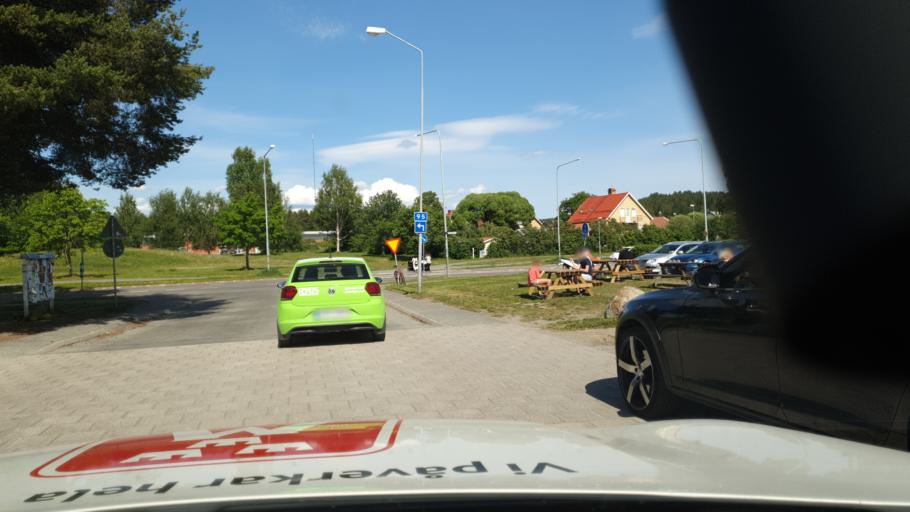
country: SE
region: Vaesterbotten
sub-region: Skelleftea Kommun
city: Viken
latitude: 64.7561
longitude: 20.9170
